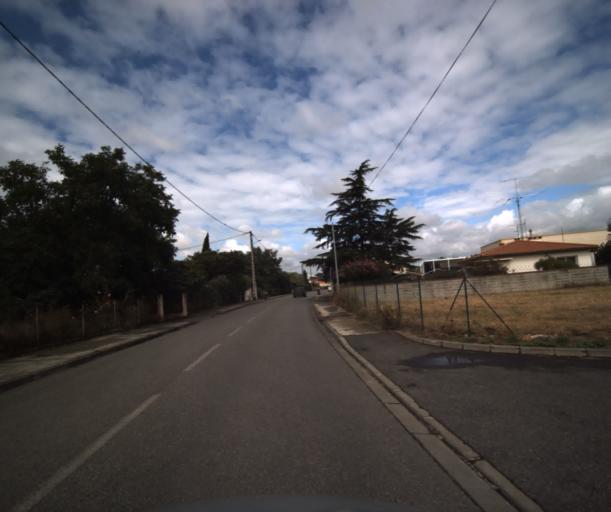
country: FR
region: Midi-Pyrenees
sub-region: Departement de la Haute-Garonne
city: Pinsaguel
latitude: 43.5277
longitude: 1.3764
